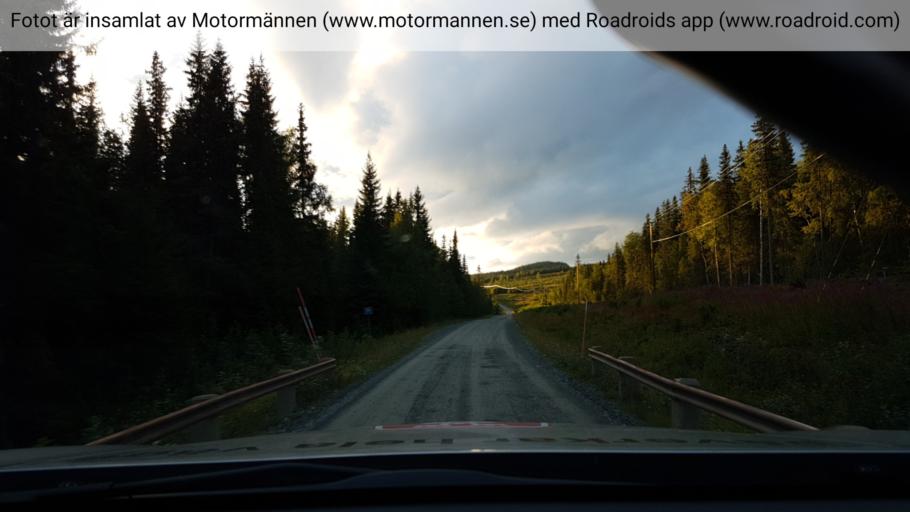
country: SE
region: Vaesterbotten
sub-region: Vilhelmina Kommun
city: Sjoberg
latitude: 65.5569
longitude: 15.3974
